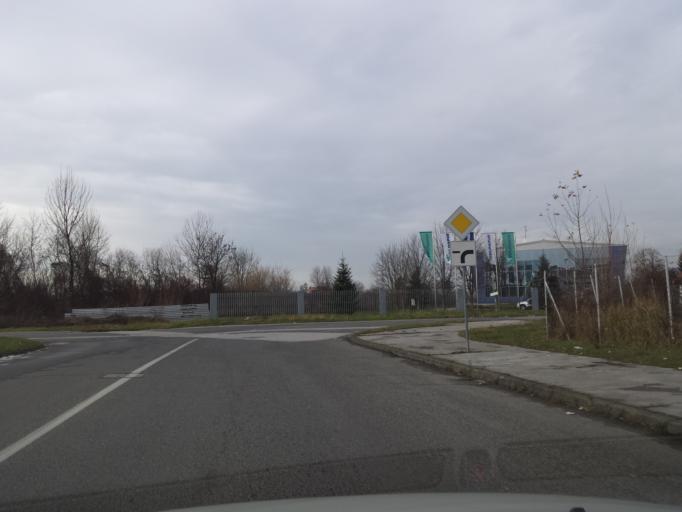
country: HR
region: Grad Zagreb
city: Jezdovec
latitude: 45.8083
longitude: 15.8451
